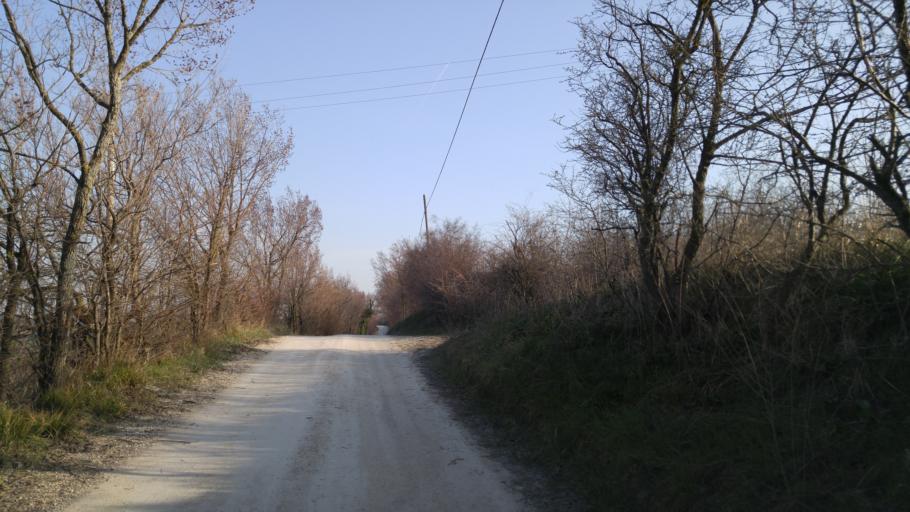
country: IT
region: The Marches
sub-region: Provincia di Pesaro e Urbino
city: Bellocchi
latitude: 43.7647
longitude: 12.9965
